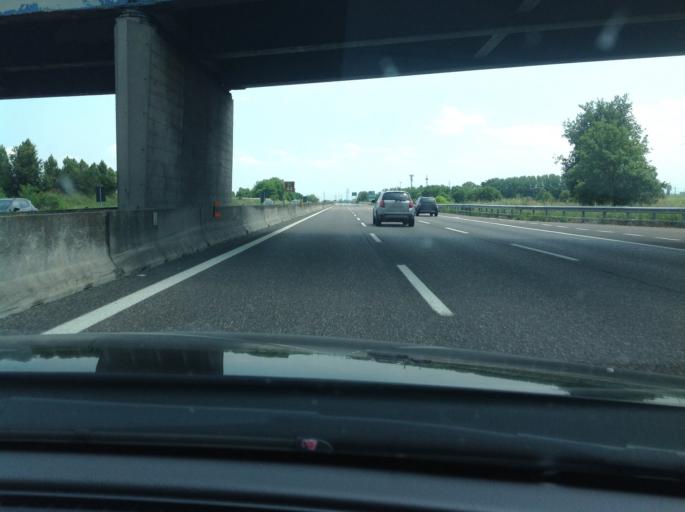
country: IT
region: Lombardy
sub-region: Provincia di Lodi
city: Somaglia
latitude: 45.1487
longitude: 9.6253
